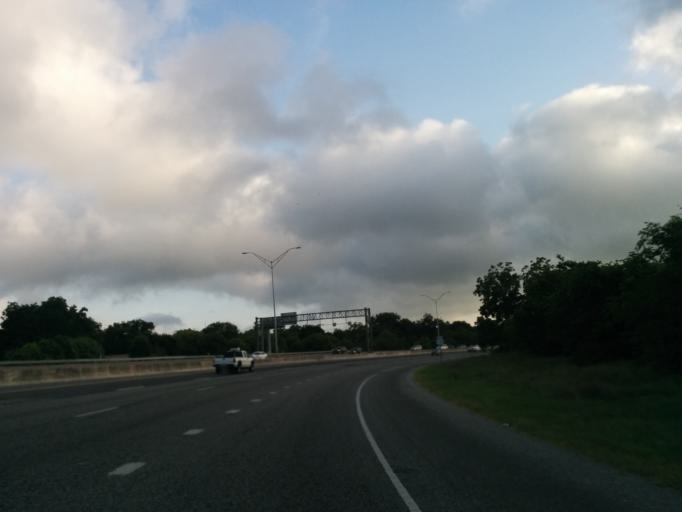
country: US
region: Texas
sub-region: Bexar County
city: San Antonio
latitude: 29.4497
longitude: -98.4836
